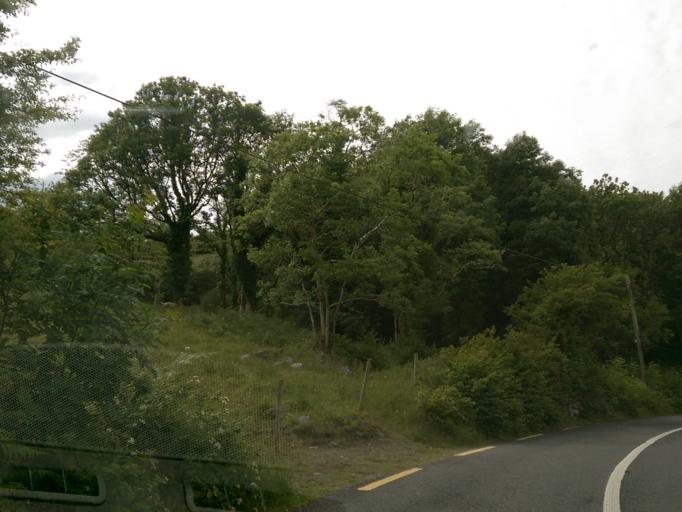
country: IE
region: Connaught
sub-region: County Galway
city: Bearna
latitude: 53.0719
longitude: -9.1874
